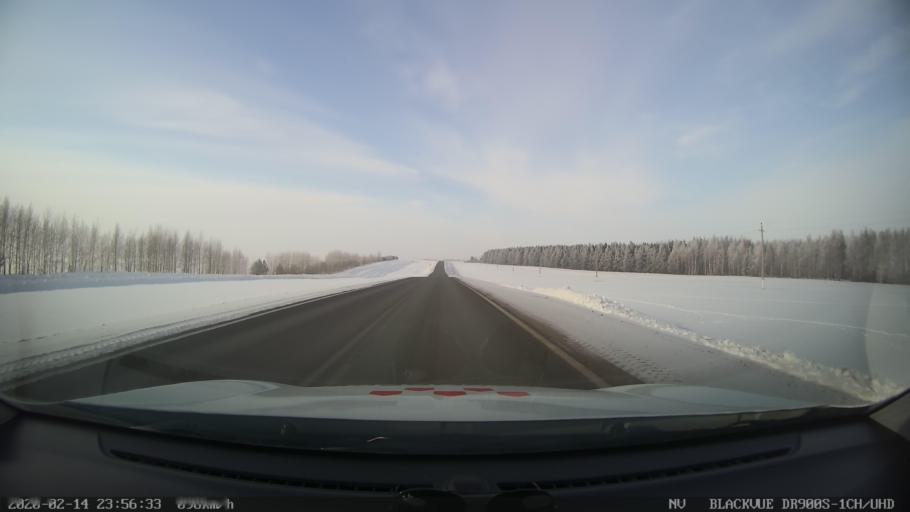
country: RU
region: Tatarstan
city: Kuybyshevskiy Zaton
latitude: 55.3259
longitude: 49.1280
